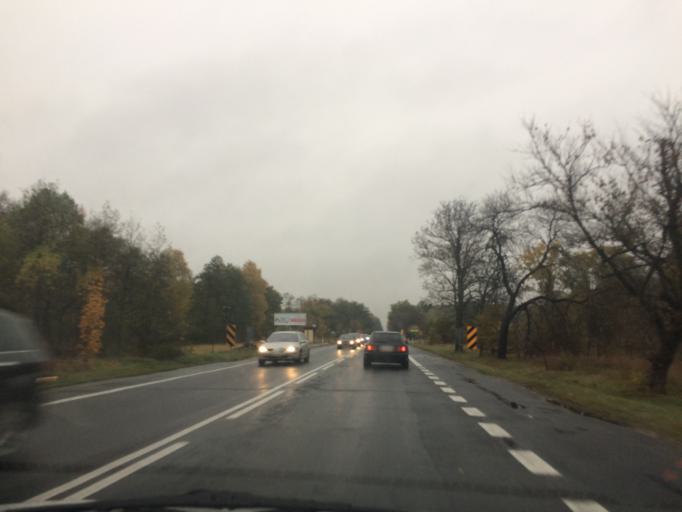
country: PL
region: Masovian Voivodeship
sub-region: Powiat otwocki
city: Kolbiel
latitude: 52.0773
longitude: 21.4455
